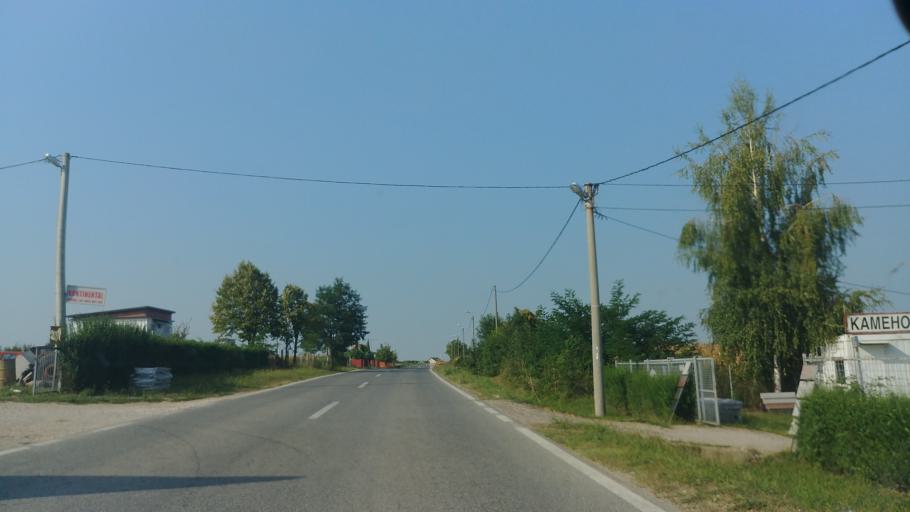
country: BA
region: Brcko
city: Brcko
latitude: 44.7760
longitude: 18.8097
